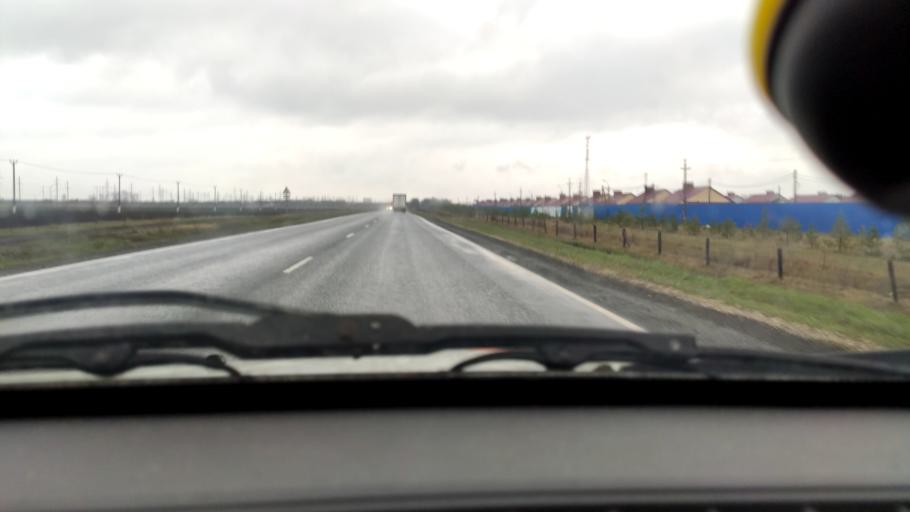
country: RU
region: Samara
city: Povolzhskiy
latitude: 53.6446
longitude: 49.6696
